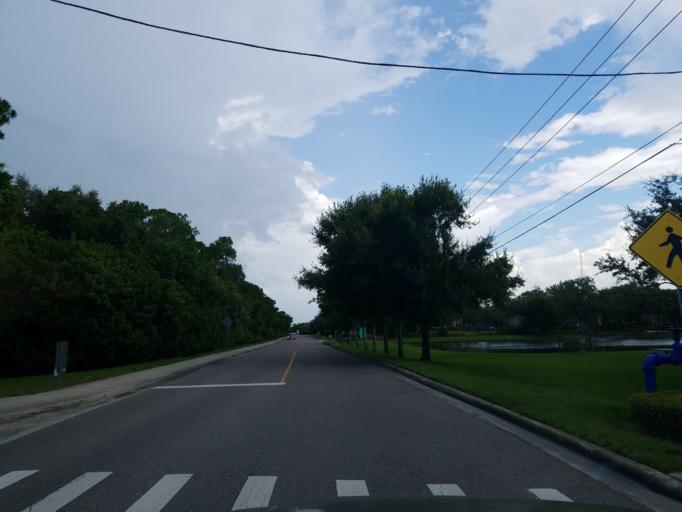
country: US
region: Florida
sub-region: Pinellas County
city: Gandy
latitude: 27.8739
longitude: -82.6377
